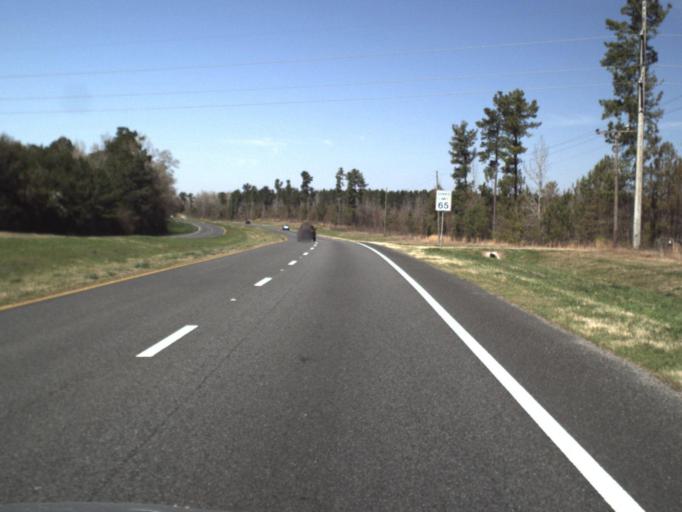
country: US
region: Florida
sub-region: Jackson County
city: Graceville
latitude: 30.9579
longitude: -85.4027
